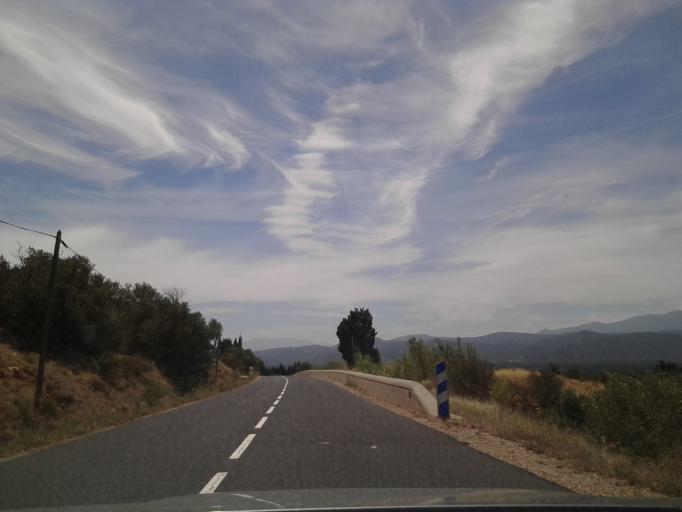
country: FR
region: Languedoc-Roussillon
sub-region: Departement des Pyrenees-Orientales
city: Millas
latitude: 42.7110
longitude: 2.6836
